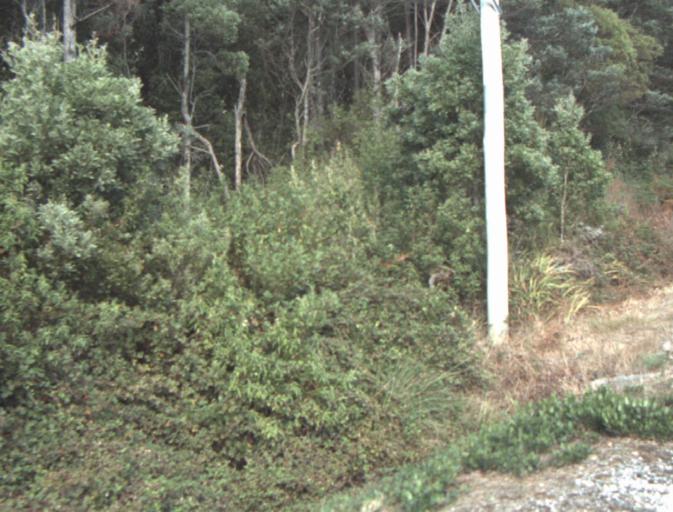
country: AU
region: Tasmania
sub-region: Launceston
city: Mayfield
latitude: -41.2801
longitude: 147.2200
